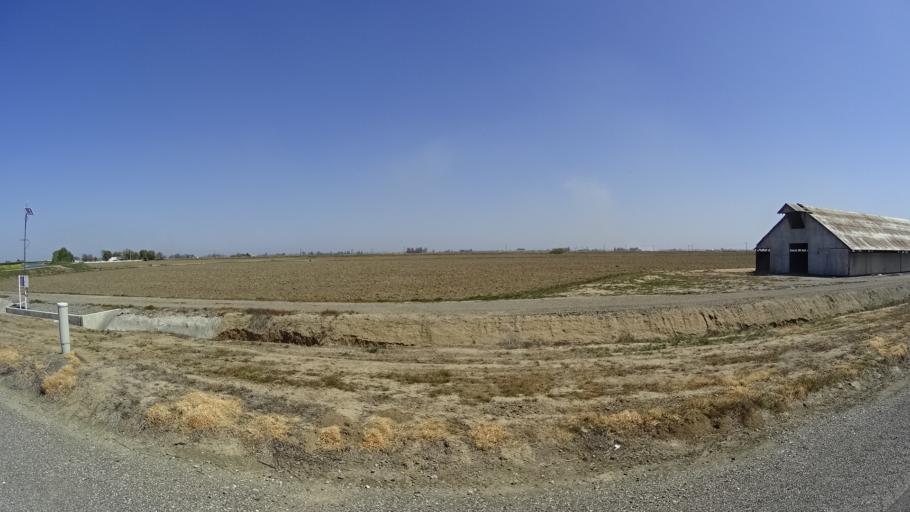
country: US
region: California
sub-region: Glenn County
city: Willows
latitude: 39.5558
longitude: -122.1370
